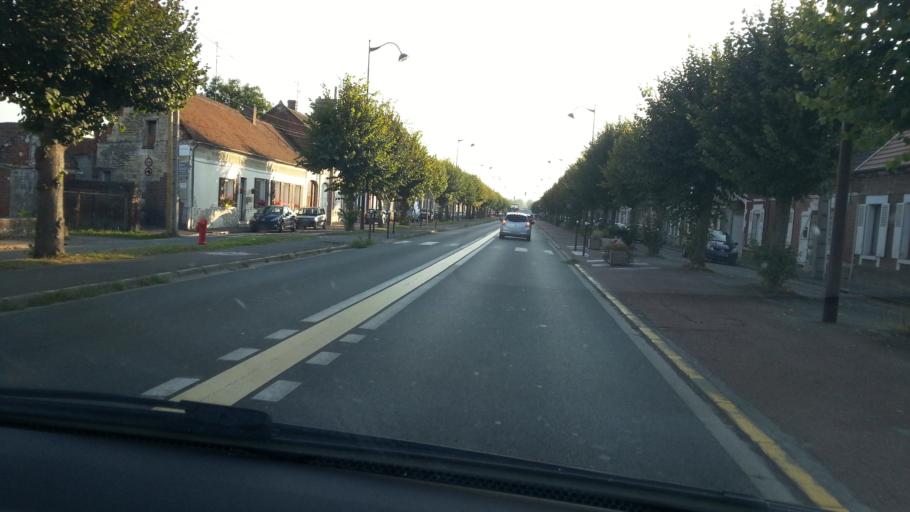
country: FR
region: Picardie
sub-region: Departement de l'Oise
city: Estrees-Saint-Denis
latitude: 49.4294
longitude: 2.6396
